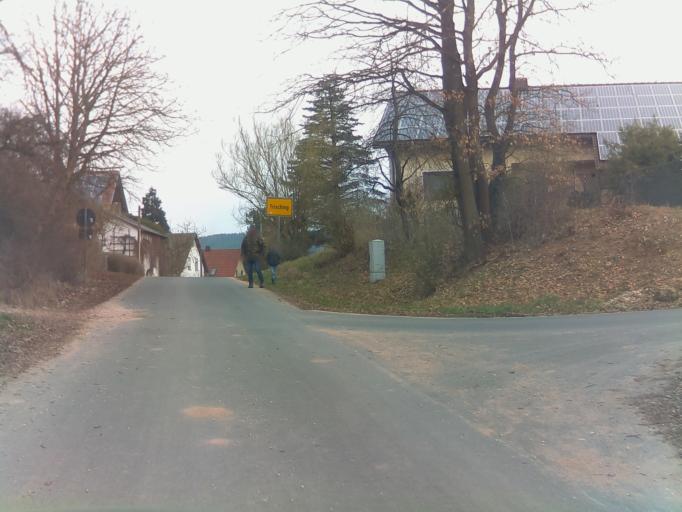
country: DE
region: Bavaria
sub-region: Upper Palatinate
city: Schmidgaden
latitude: 49.4301
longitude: 12.0532
